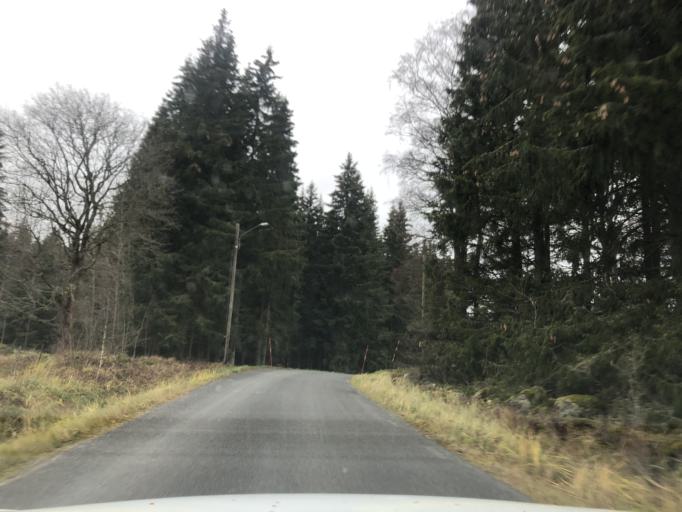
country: SE
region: Vaestra Goetaland
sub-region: Ulricehamns Kommun
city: Ulricehamn
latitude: 57.8434
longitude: 13.6403
